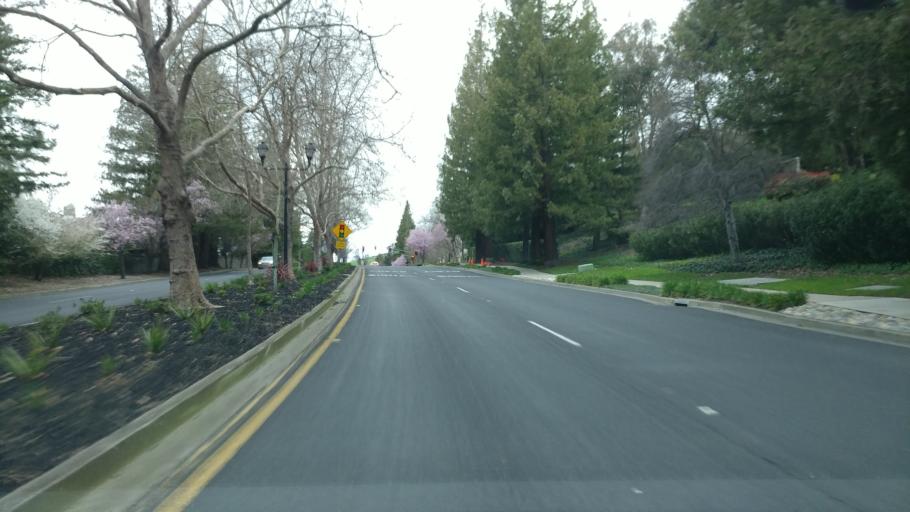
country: US
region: California
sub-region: Contra Costa County
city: Blackhawk
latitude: 37.8019
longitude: -121.9215
